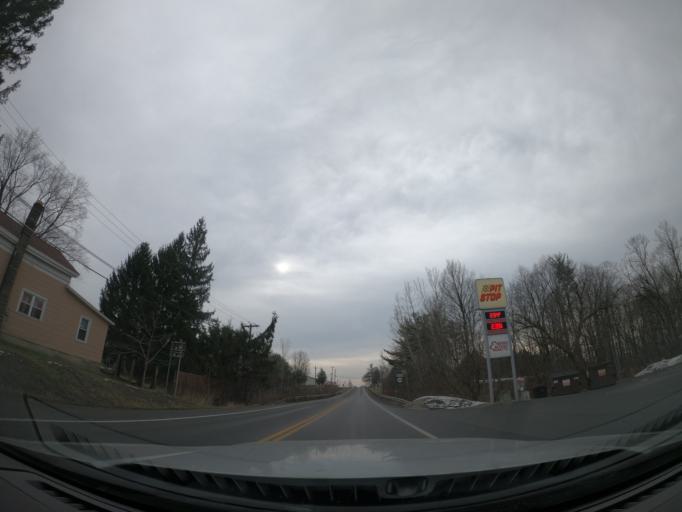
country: US
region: New York
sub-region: Cayuga County
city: Moravia
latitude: 42.6679
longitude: -76.5279
